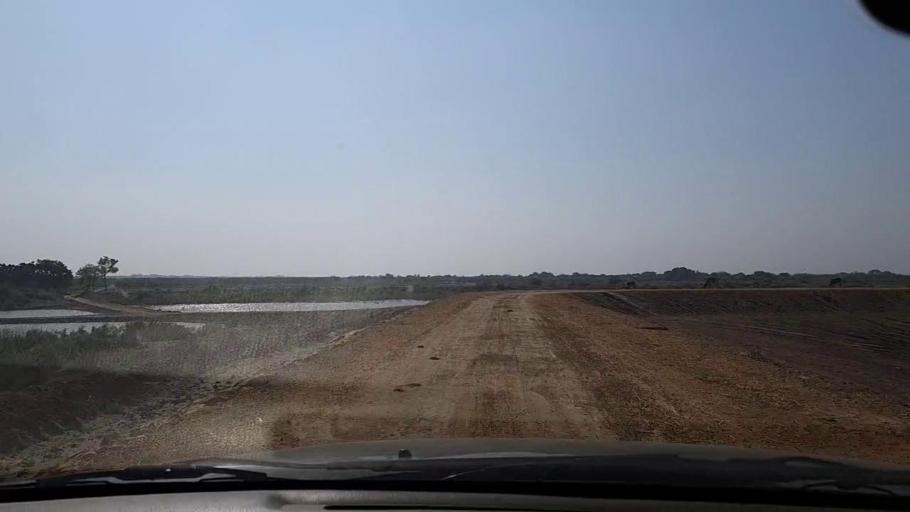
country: PK
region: Sindh
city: Chuhar Jamali
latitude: 24.4560
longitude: 67.8763
